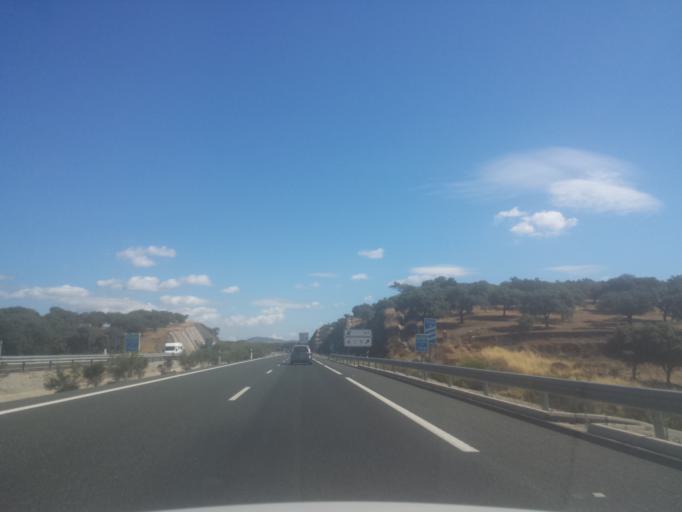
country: ES
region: Andalusia
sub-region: Provincia de Huelva
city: Santa Olalla del Cala
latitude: 37.8986
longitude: -6.2147
